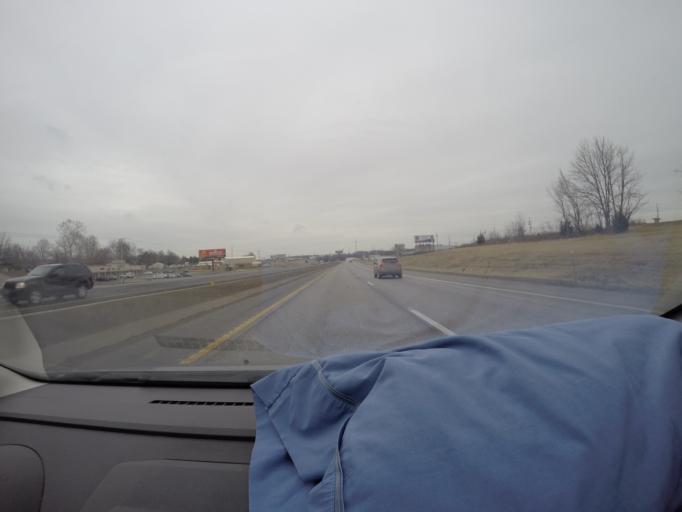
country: US
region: Missouri
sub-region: Warren County
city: Warrenton
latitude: 38.8198
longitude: -91.1336
